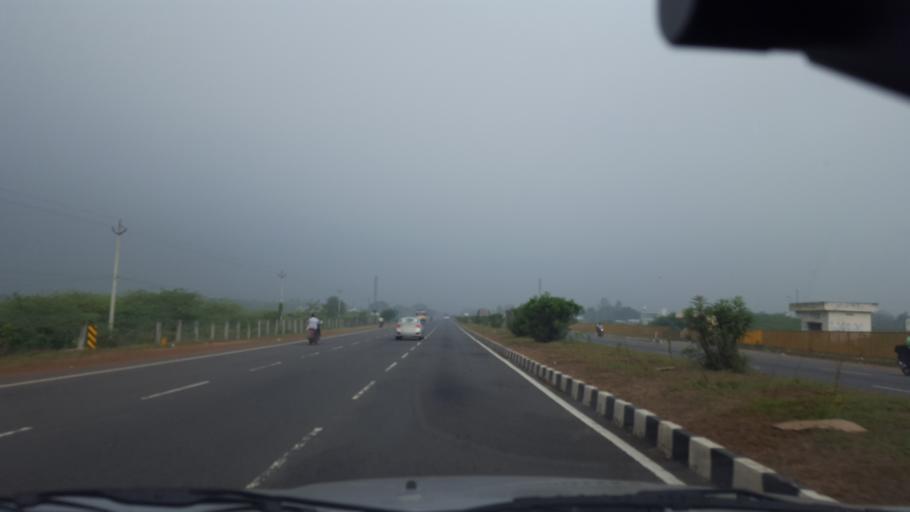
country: IN
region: Andhra Pradesh
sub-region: Prakasam
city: Ongole
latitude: 15.5811
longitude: 80.0404
